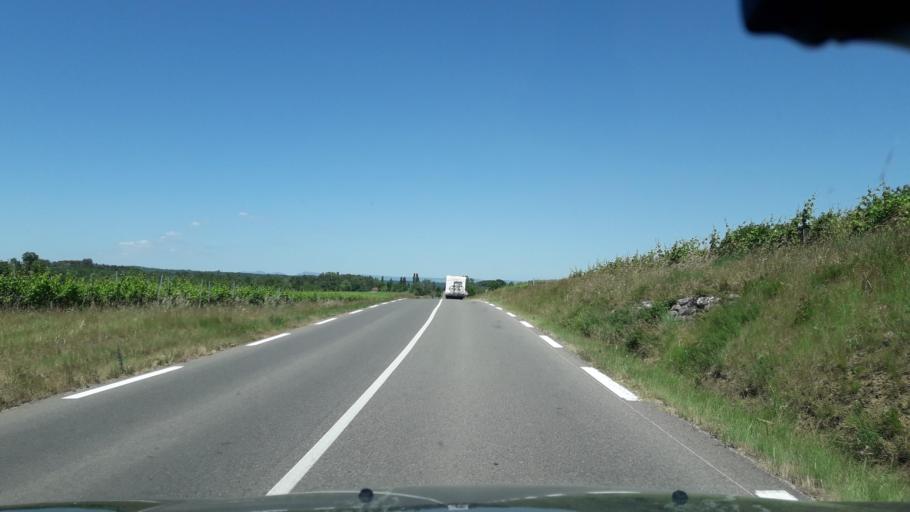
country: FR
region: Rhone-Alpes
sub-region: Departement de l'Ardeche
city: Lablachere
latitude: 44.3938
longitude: 4.2633
